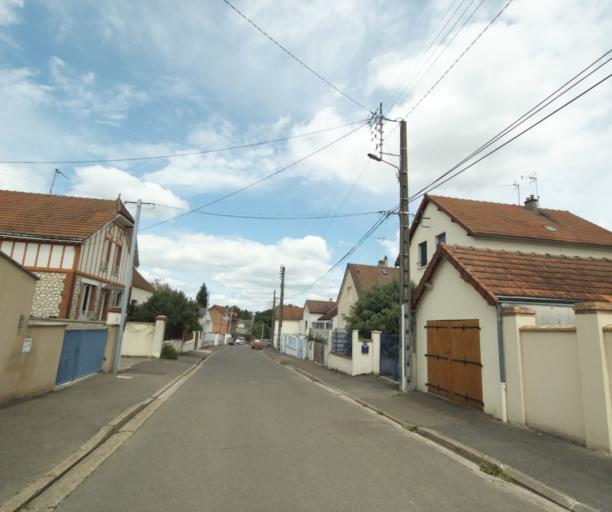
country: FR
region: Centre
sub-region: Departement d'Eure-et-Loir
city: Luce
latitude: 48.4420
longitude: 1.4679
